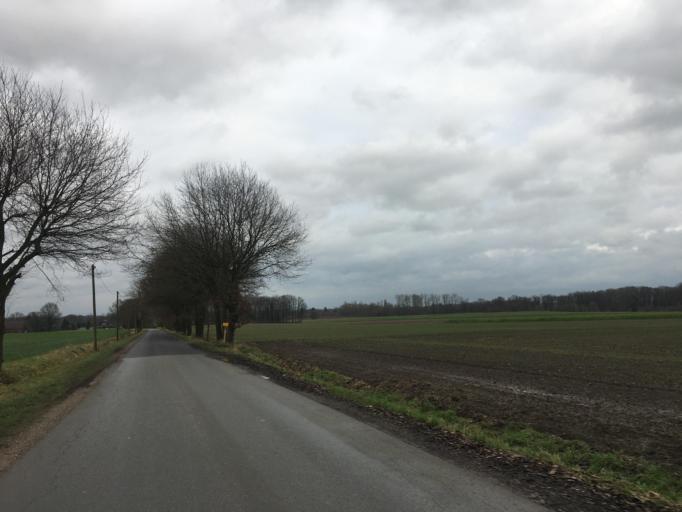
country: DE
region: North Rhine-Westphalia
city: Oer-Erkenschwick
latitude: 51.6784
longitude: 7.3032
